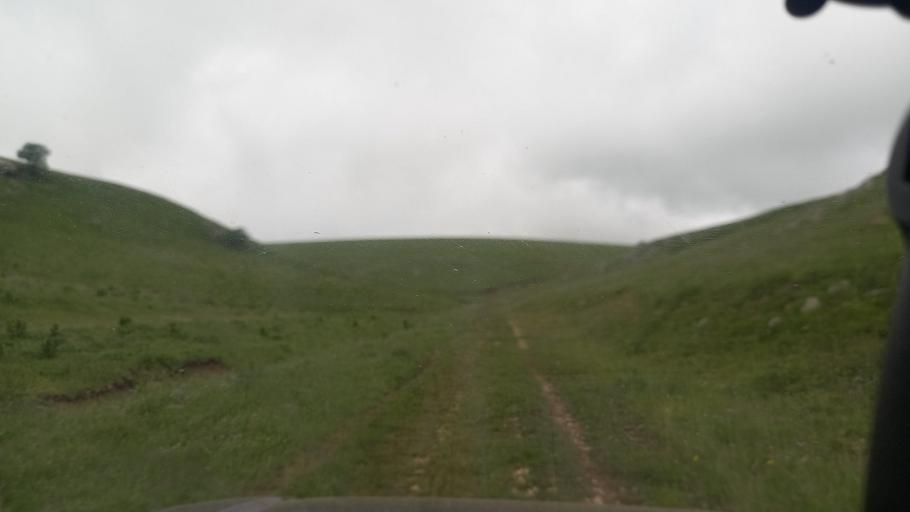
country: RU
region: Karachayevo-Cherkesiya
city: Pregradnaya
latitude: 43.9852
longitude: 41.3047
